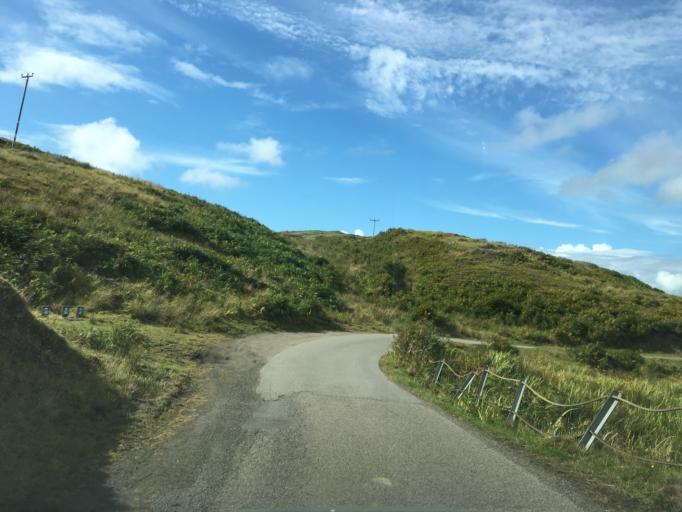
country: GB
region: Scotland
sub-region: Argyll and Bute
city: Oban
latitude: 56.2538
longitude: -5.6357
